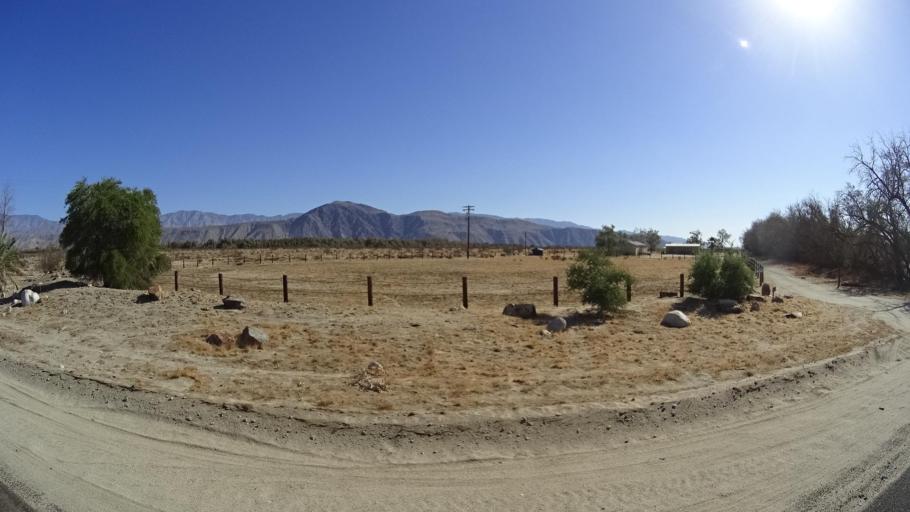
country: US
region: California
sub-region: San Diego County
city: Borrego Springs
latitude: 33.2937
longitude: -116.3786
